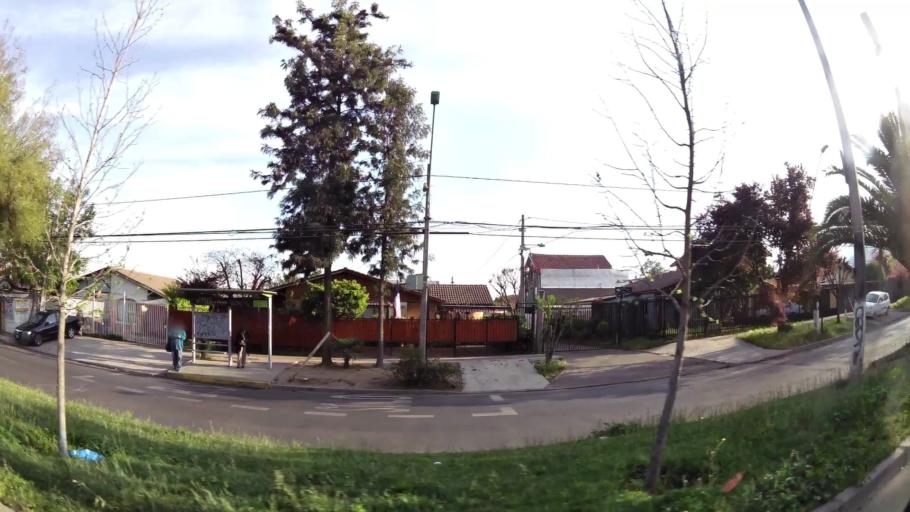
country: CL
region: Santiago Metropolitan
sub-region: Provincia de Cordillera
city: Puente Alto
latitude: -33.5593
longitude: -70.5575
